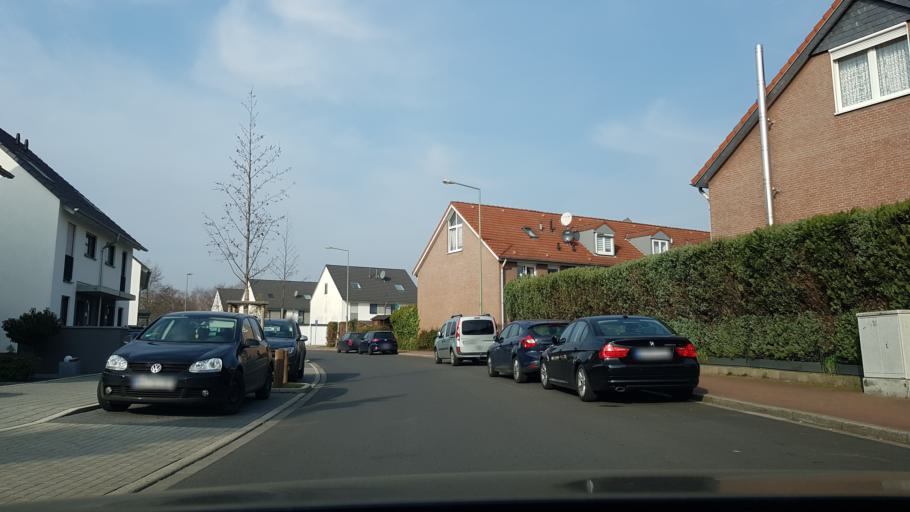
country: DE
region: North Rhine-Westphalia
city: Meiderich
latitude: 51.5109
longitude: 6.7952
